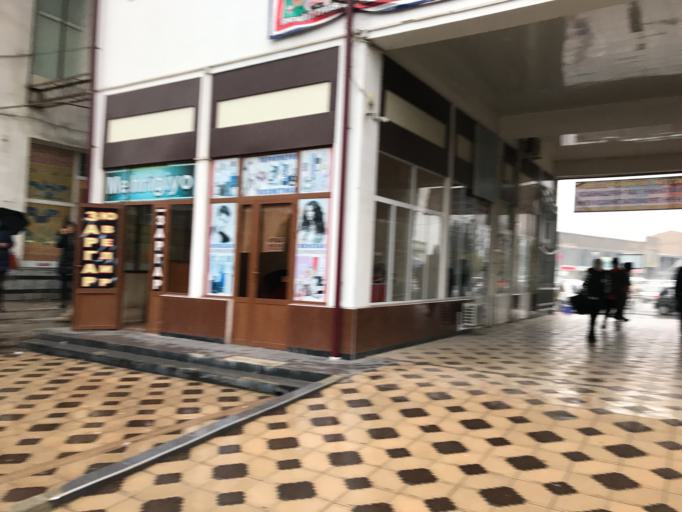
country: UZ
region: Toshkent
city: Yangiyul
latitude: 41.1151
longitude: 69.0560
